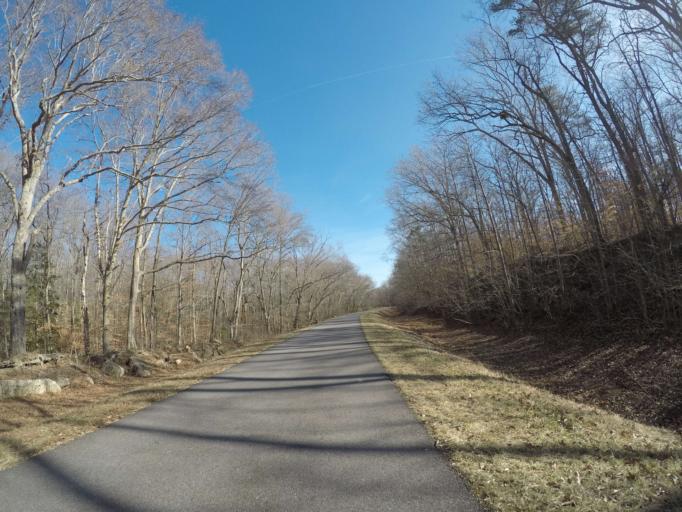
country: US
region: Maryland
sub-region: Charles County
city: Bennsville
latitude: 38.5959
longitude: -76.9841
